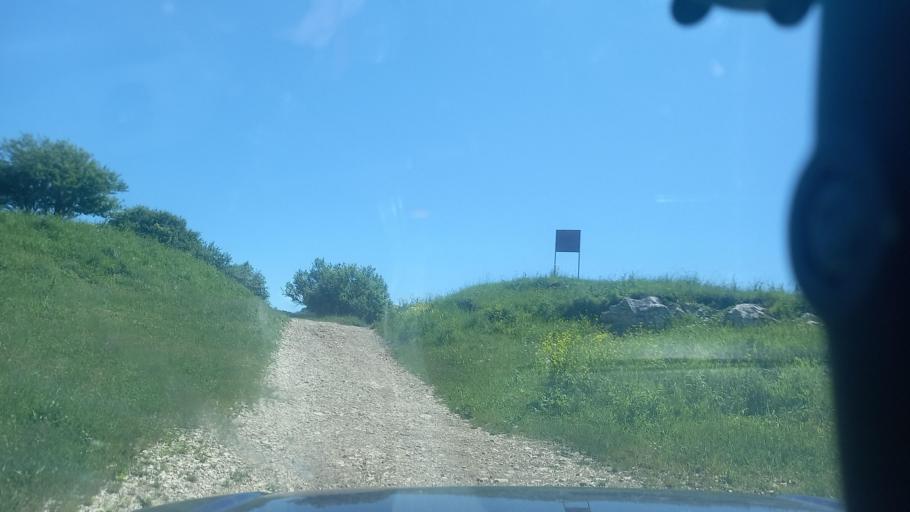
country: RU
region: Karachayevo-Cherkesiya
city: Pregradnaya
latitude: 44.1026
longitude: 41.1171
